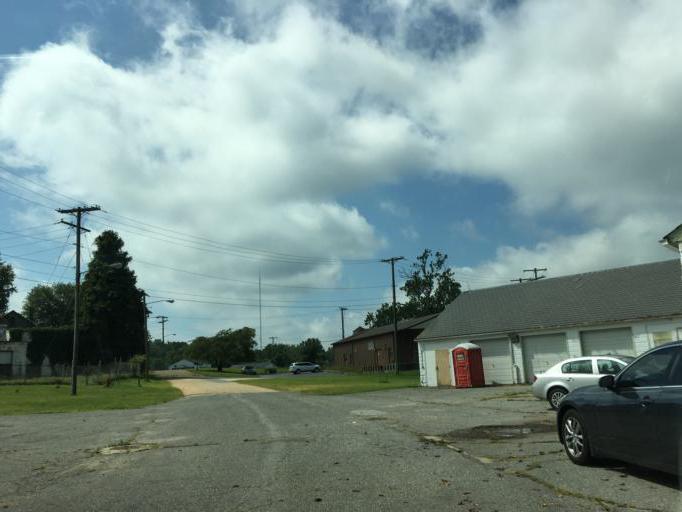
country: US
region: Maryland
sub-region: Anne Arundel County
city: Crownsville
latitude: 39.0228
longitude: -76.6032
